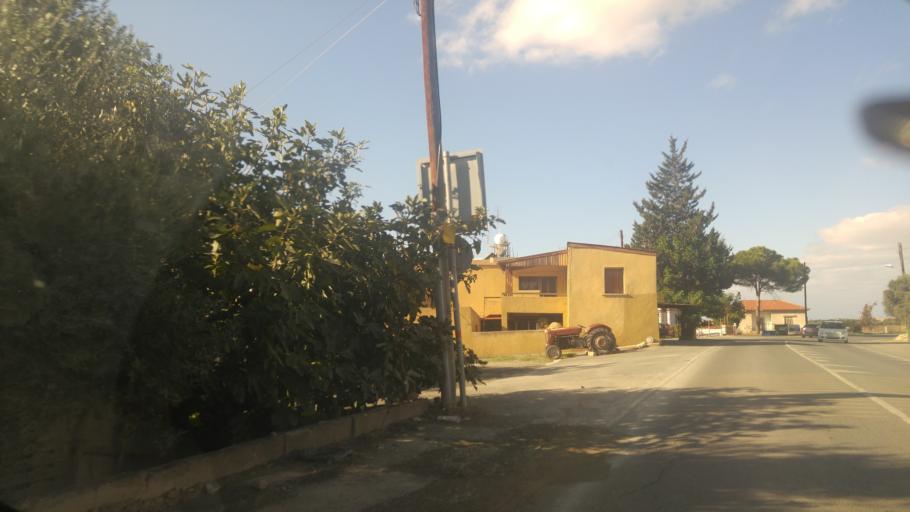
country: CY
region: Larnaka
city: Kolossi
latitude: 34.6707
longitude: 32.9323
